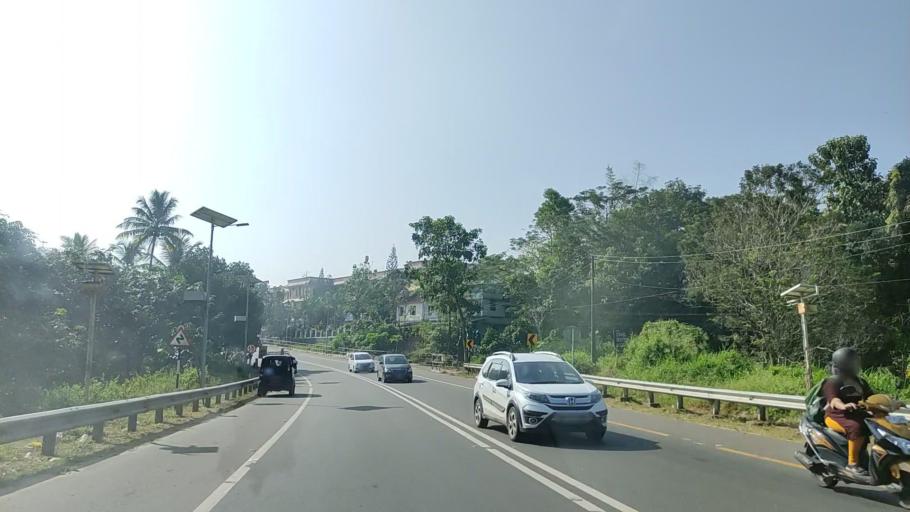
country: IN
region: Kerala
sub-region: Kollam
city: Punalur
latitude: 8.8895
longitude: 76.8673
